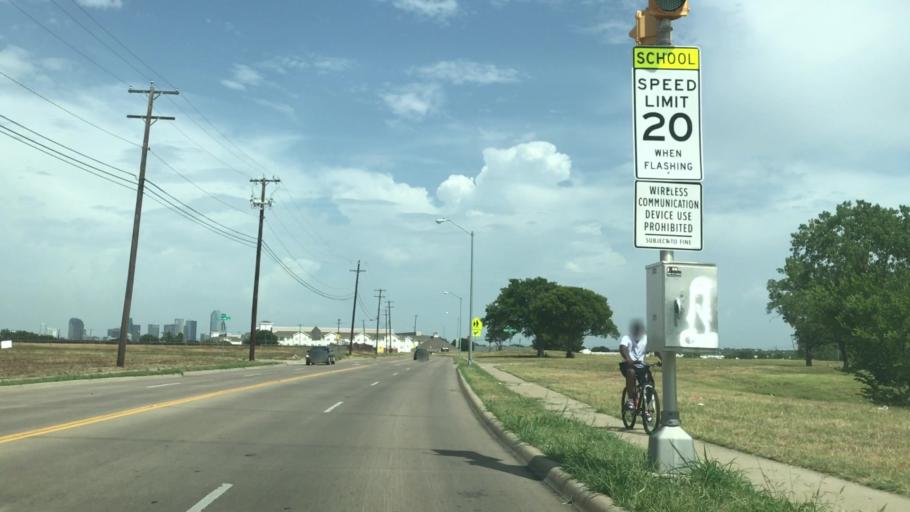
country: US
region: Texas
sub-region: Dallas County
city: Cockrell Hill
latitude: 32.7862
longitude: -96.8684
